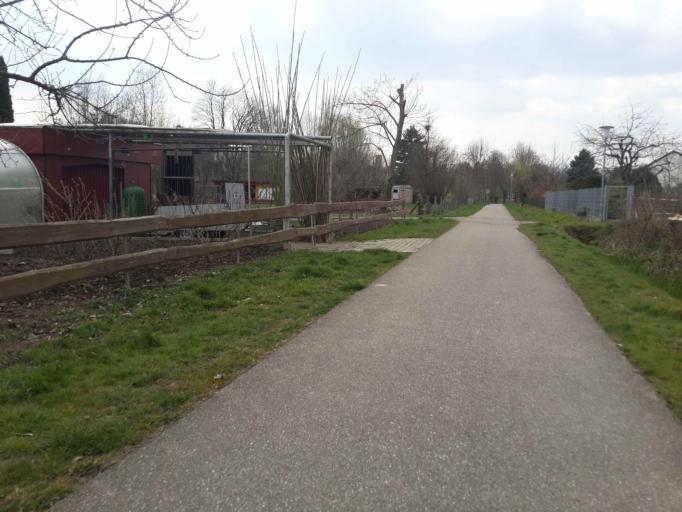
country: DE
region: Baden-Wuerttemberg
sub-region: Karlsruhe Region
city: Balzfeld
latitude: 49.2293
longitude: 8.7834
